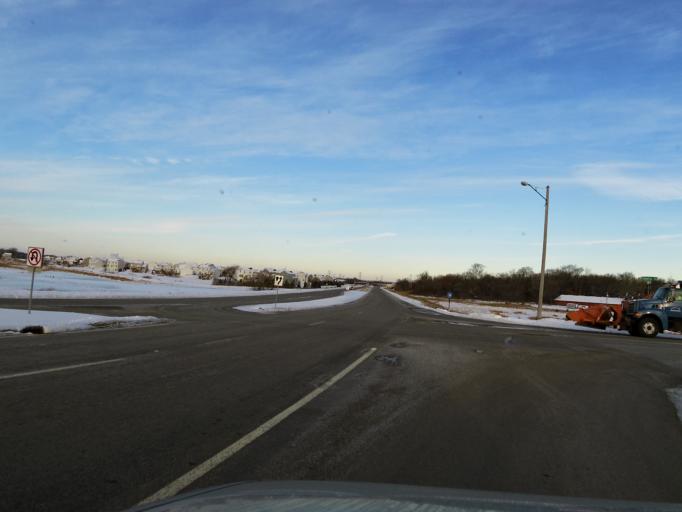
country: US
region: Minnesota
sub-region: Scott County
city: Prior Lake
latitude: 44.7674
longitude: -93.4058
